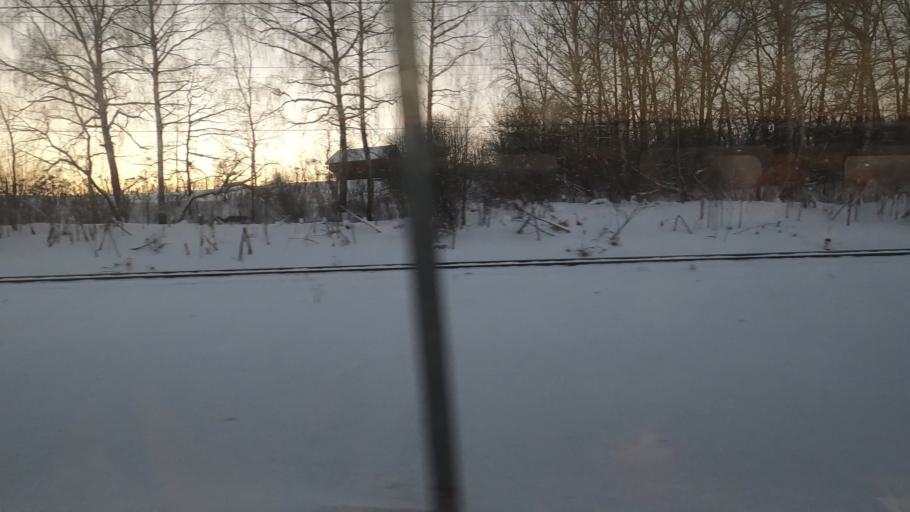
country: RU
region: Moskovskaya
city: Yermolino
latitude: 56.1543
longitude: 37.5020
